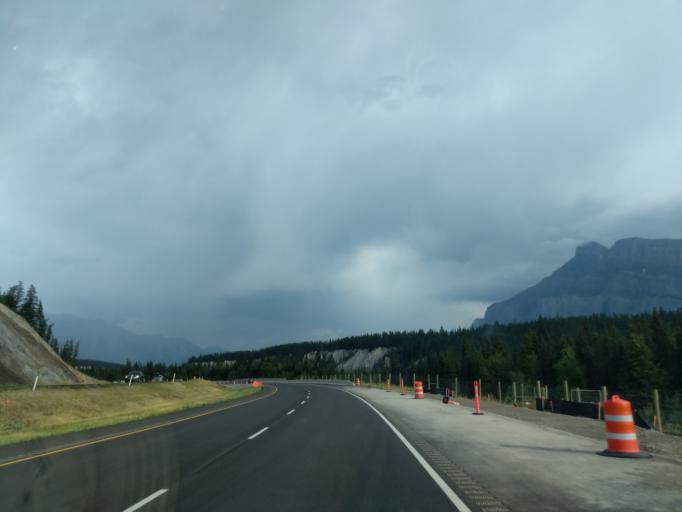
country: CA
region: Alberta
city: Banff
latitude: 51.2036
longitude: -115.5204
